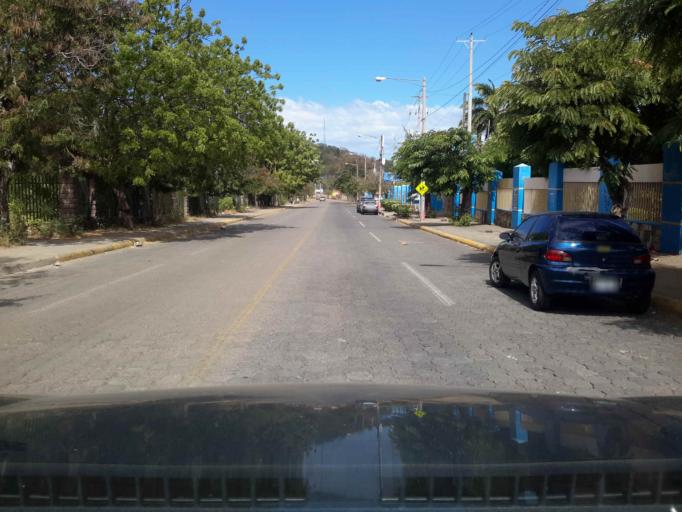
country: NI
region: Managua
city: Managua
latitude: 12.1309
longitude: -86.2710
